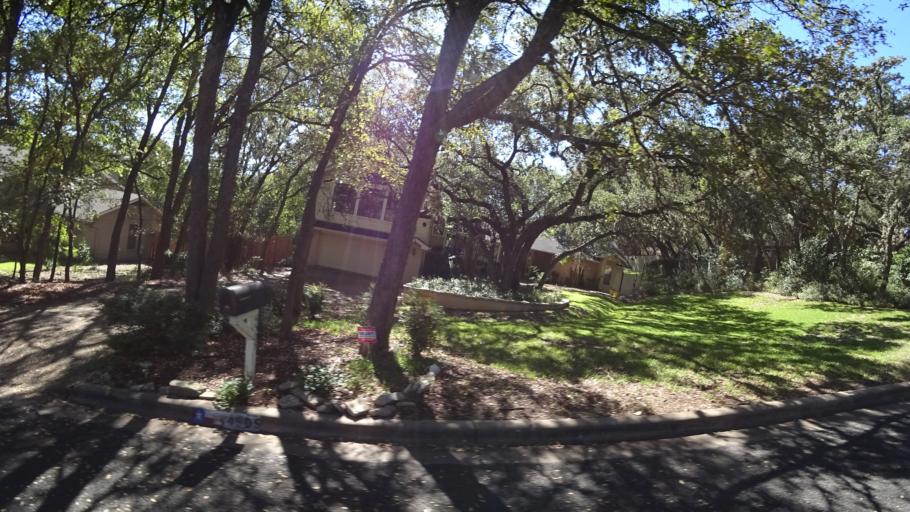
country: US
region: Texas
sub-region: Travis County
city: West Lake Hills
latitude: 30.3423
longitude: -97.7779
